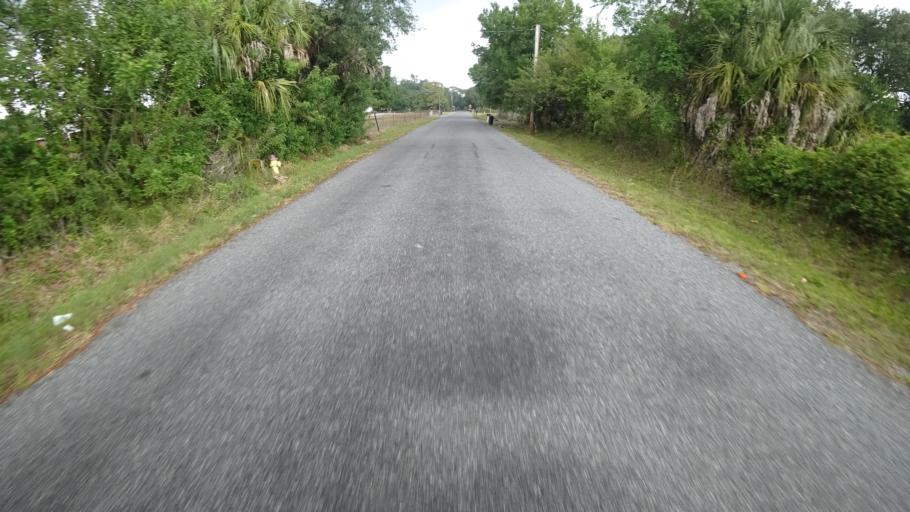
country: US
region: Florida
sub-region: Manatee County
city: Samoset
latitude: 27.4770
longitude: -82.5037
